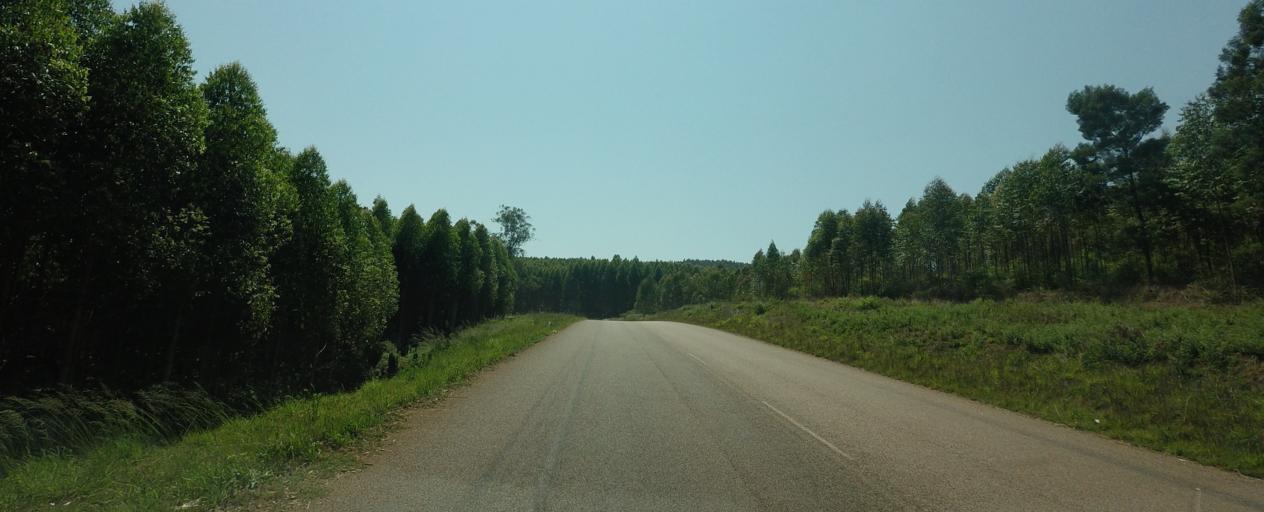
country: ZA
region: Mpumalanga
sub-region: Ehlanzeni District
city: Graksop
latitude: -25.0754
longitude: 30.8006
